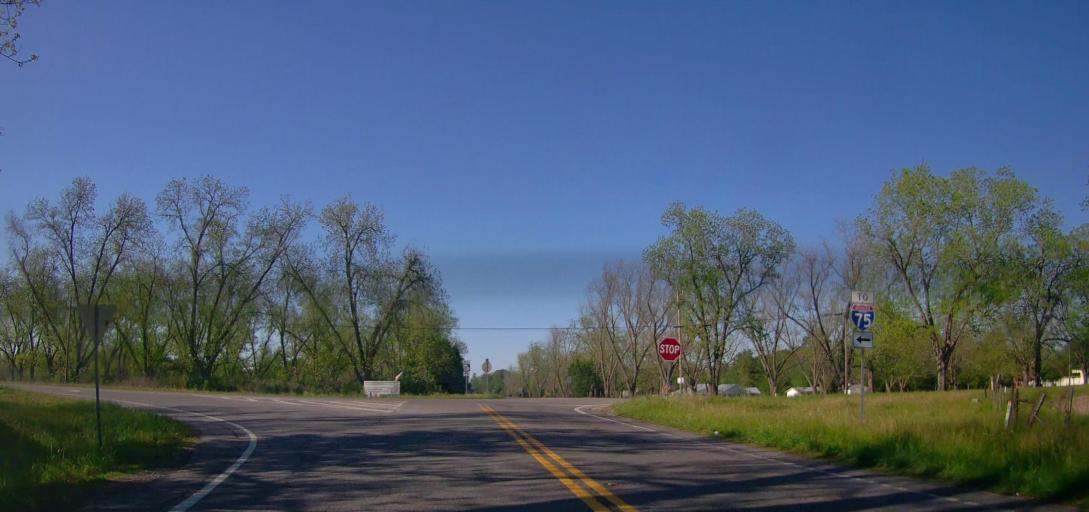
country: US
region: Georgia
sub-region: Ben Hill County
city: Fitzgerald
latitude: 31.7176
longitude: -83.3101
